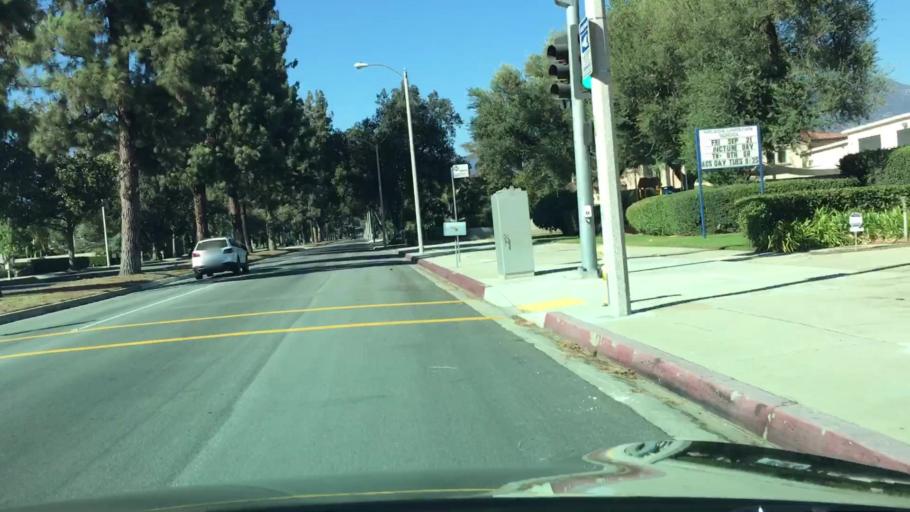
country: US
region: California
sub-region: Los Angeles County
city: North El Monte
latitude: 34.1173
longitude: -118.0309
